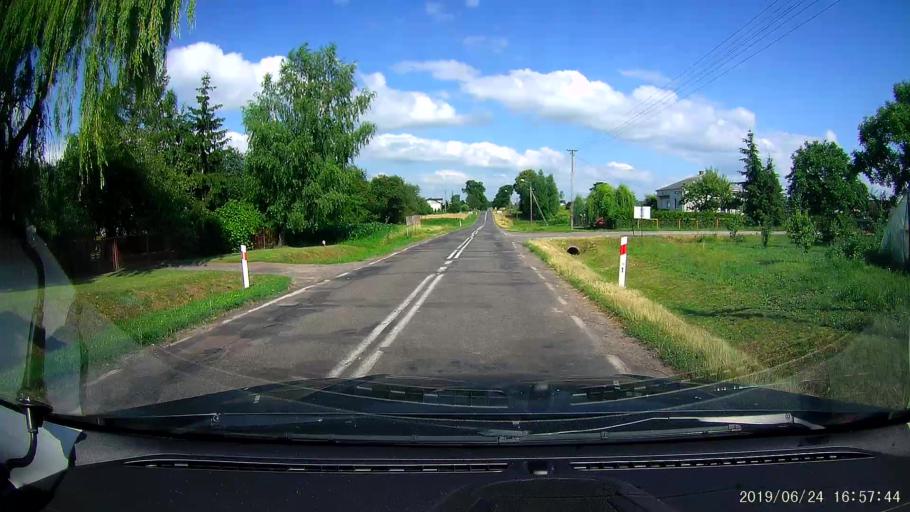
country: PL
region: Lublin Voivodeship
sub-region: Powiat tomaszowski
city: Telatyn
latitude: 50.5260
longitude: 23.8646
